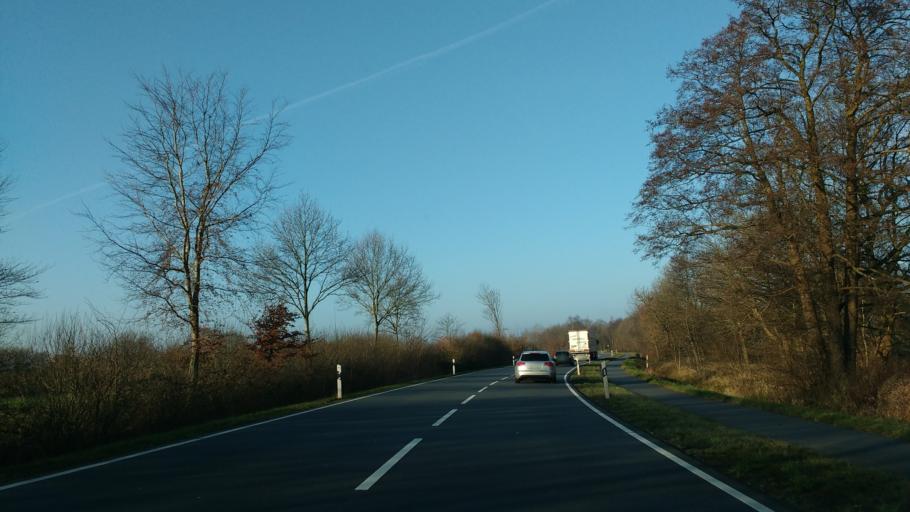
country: DE
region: Schleswig-Holstein
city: Hadenfeld
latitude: 54.0305
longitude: 9.4570
